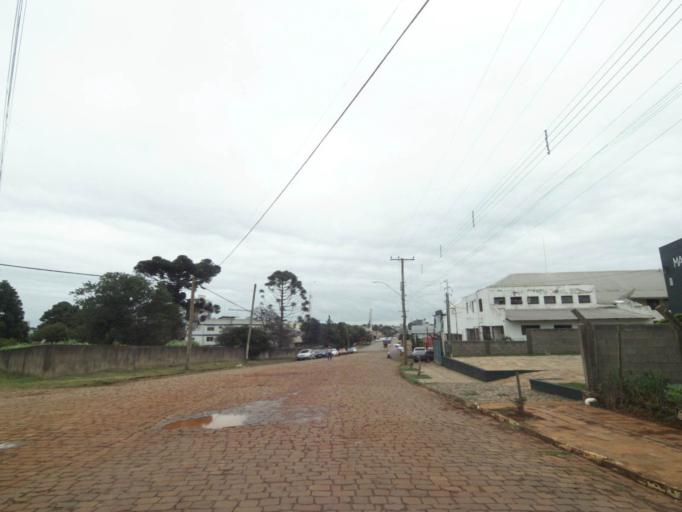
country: BR
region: Rio Grande do Sul
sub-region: Lagoa Vermelha
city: Lagoa Vermelha
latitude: -28.2171
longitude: -51.5196
